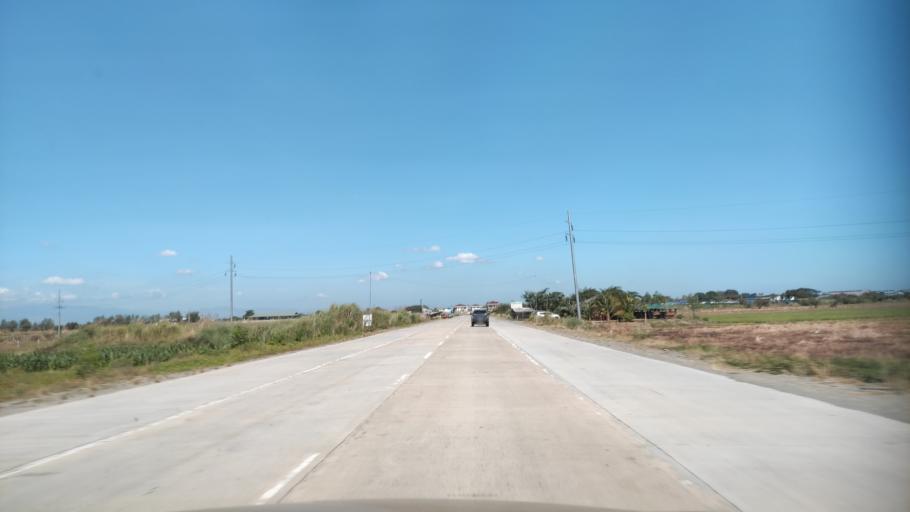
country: PH
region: Central Luzon
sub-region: Province of Tarlac
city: Salcedo
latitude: 15.8701
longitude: 120.6102
